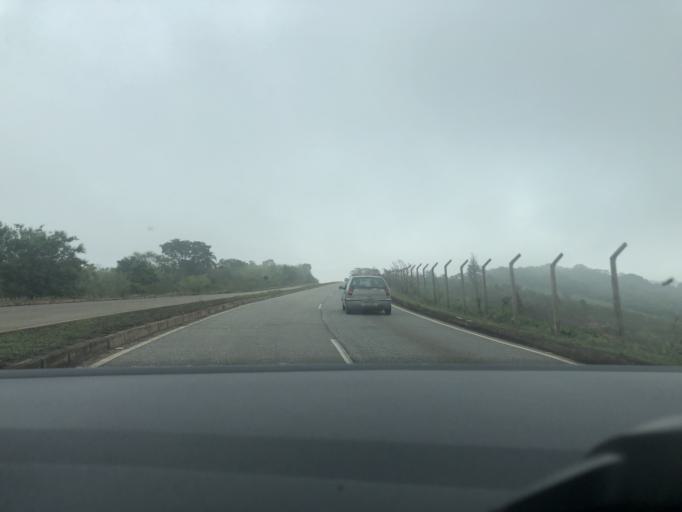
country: BR
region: Minas Gerais
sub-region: Congonhas
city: Congonhas
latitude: -20.5943
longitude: -43.9497
